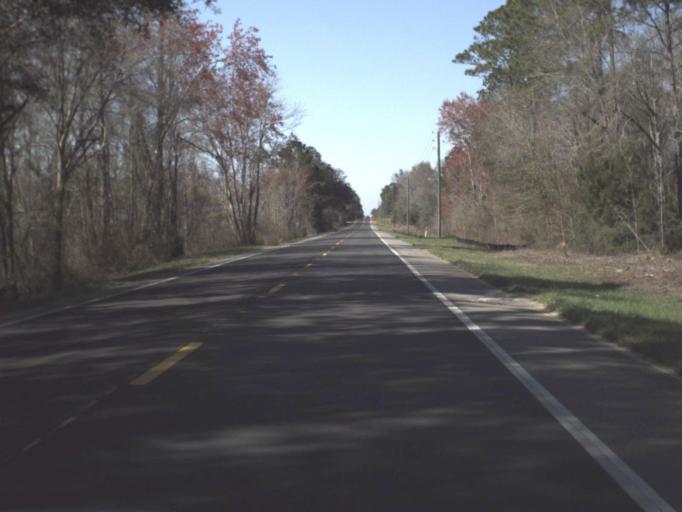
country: US
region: Florida
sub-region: Jackson County
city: Marianna
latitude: 30.6732
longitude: -85.1703
